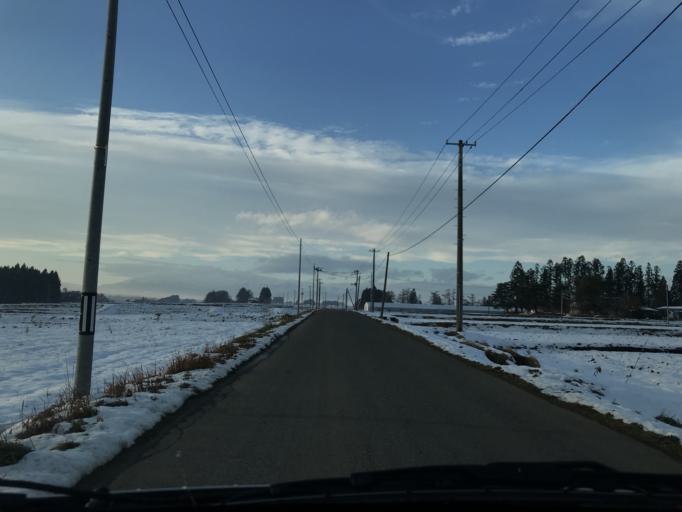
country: JP
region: Iwate
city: Mizusawa
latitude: 39.0463
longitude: 141.1089
